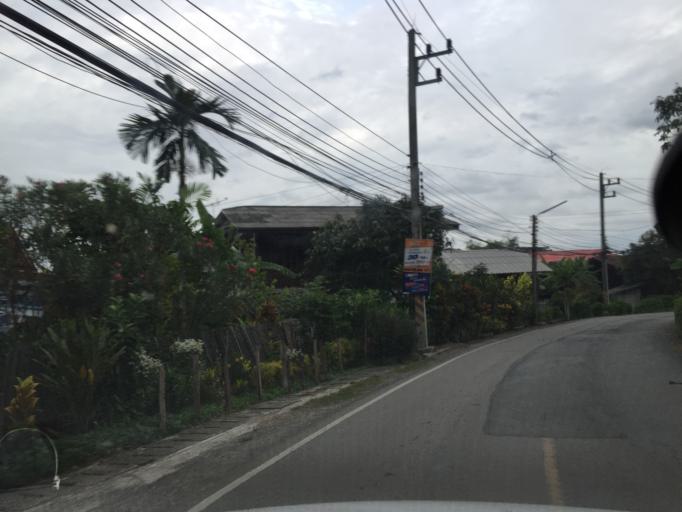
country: TH
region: Chiang Mai
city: Mae On
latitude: 18.8310
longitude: 99.1845
